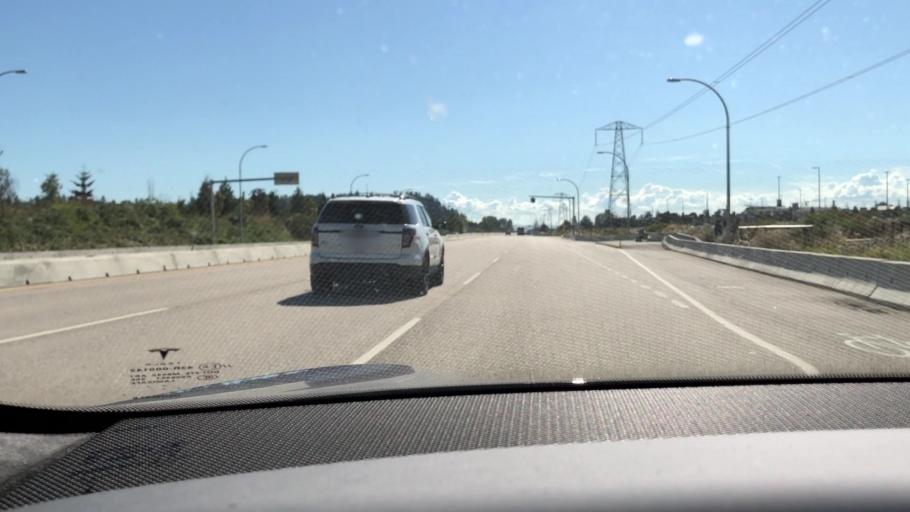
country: US
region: Washington
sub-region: Whatcom County
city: Point Roberts
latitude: 49.0373
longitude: -123.0805
